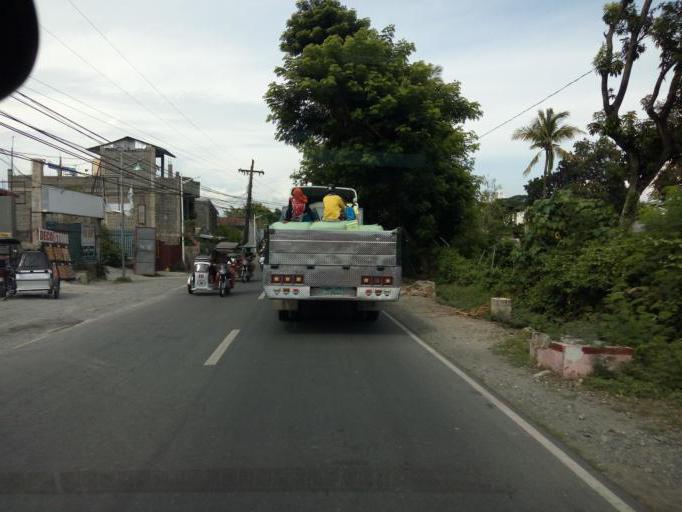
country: PH
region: Ilocos
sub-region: Province of Pangasinan
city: Rosales
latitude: 15.8939
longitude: 120.6372
